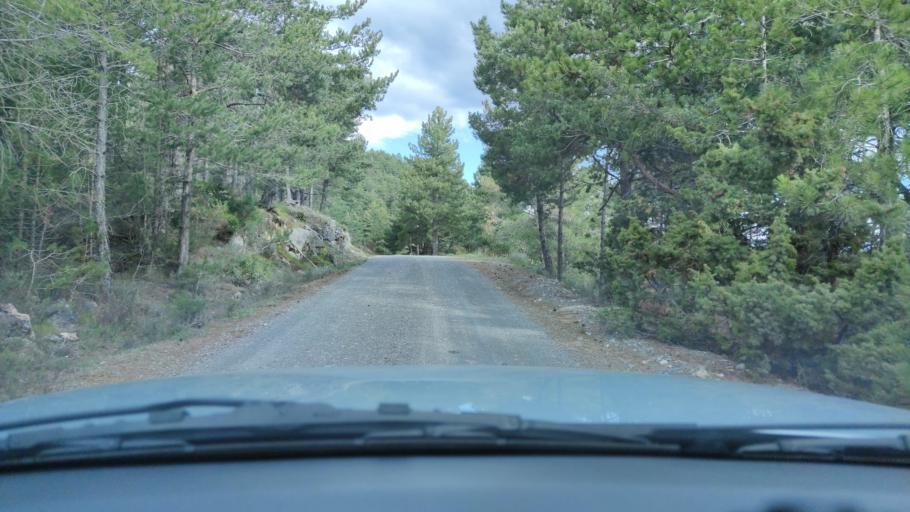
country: ES
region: Catalonia
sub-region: Provincia de Lleida
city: Coll de Nargo
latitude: 42.2434
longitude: 1.4103
